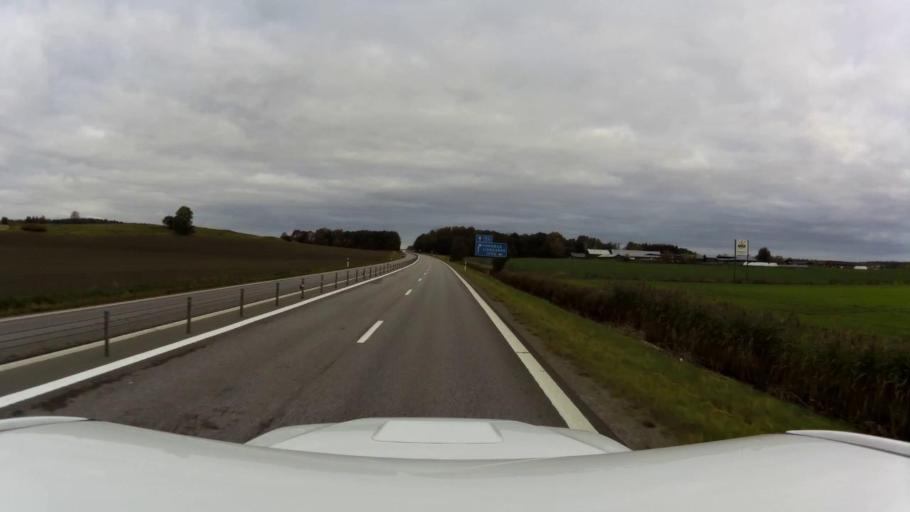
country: SE
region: OEstergoetland
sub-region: Linkopings Kommun
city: Ljungsbro
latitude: 58.4821
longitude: 15.4832
